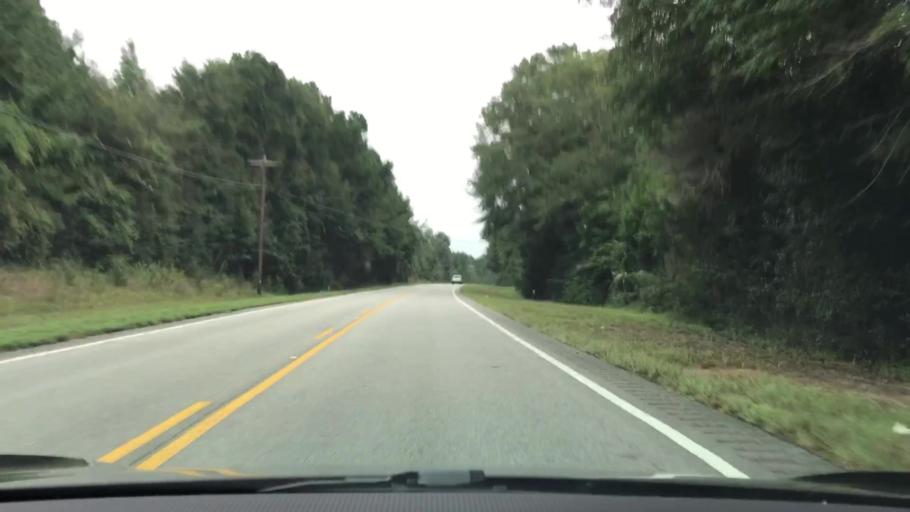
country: US
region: Alabama
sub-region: Coffee County
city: Elba
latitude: 31.4657
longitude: -86.0660
